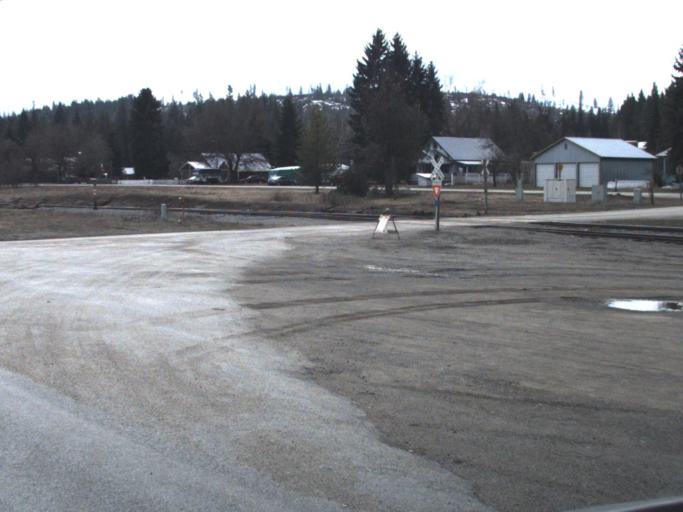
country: US
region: Washington
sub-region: Pend Oreille County
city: Newport
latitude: 48.2475
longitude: -117.2388
